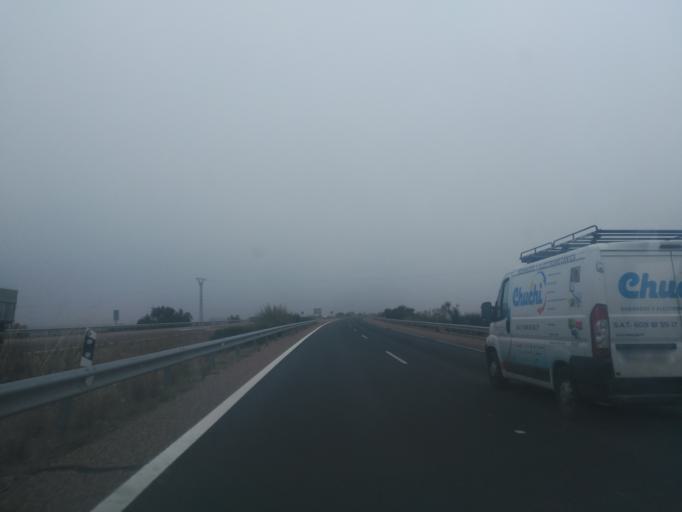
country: ES
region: Castille and Leon
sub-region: Provincia de Salamanca
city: Pajares de la Laguna
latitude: 41.0977
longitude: -5.5003
